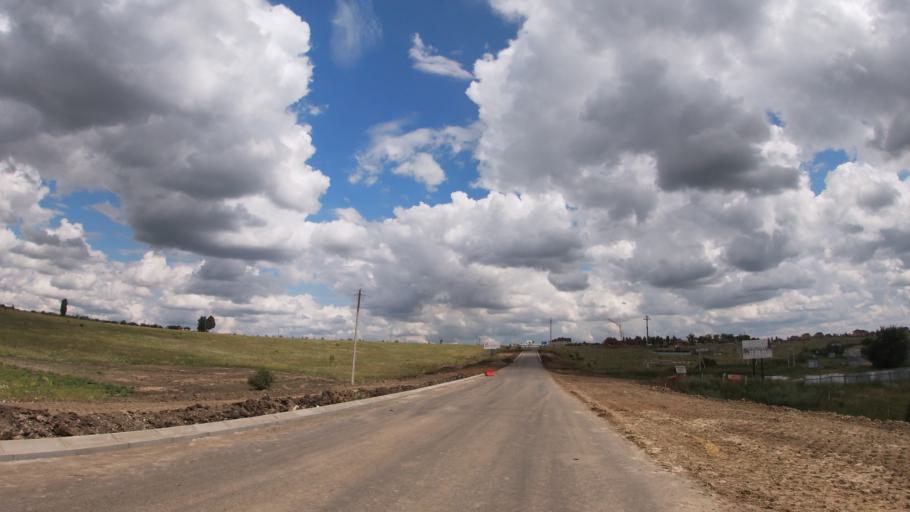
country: RU
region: Belgorod
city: Mayskiy
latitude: 50.5241
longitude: 36.5126
